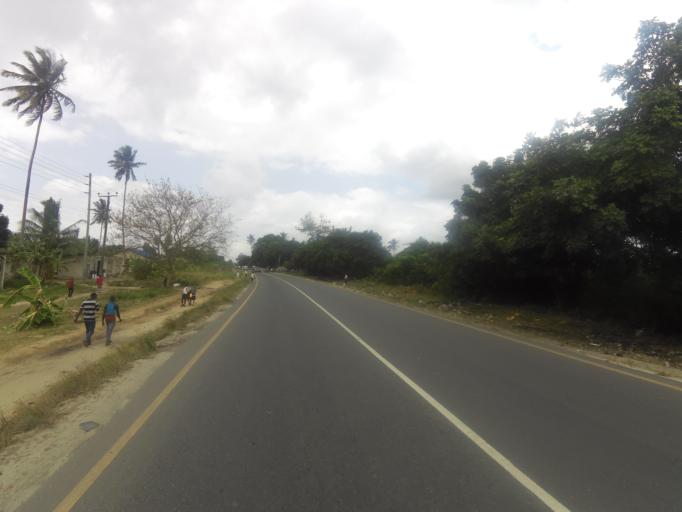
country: TZ
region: Pwani
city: Vikindu
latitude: -6.9746
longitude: 39.2867
